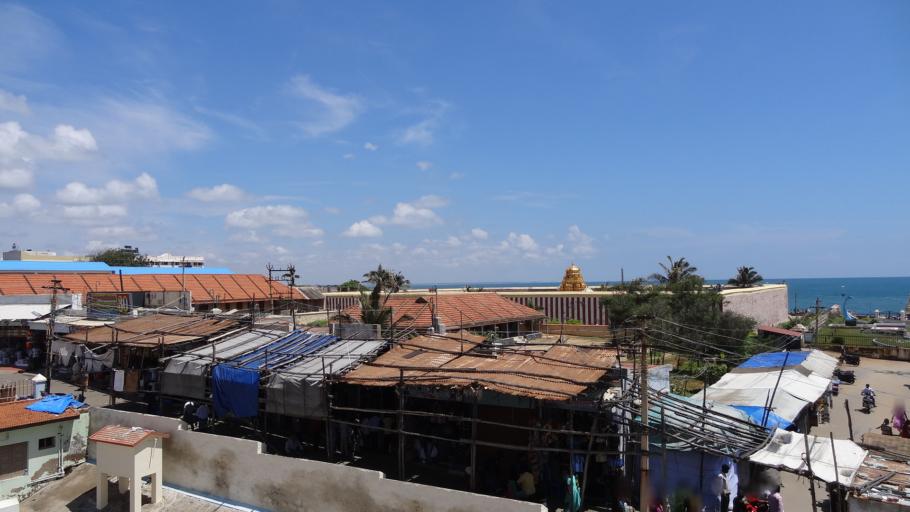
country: IN
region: Tamil Nadu
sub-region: Kanniyakumari
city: Kanniyakumari
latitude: 8.0788
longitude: 77.5500
